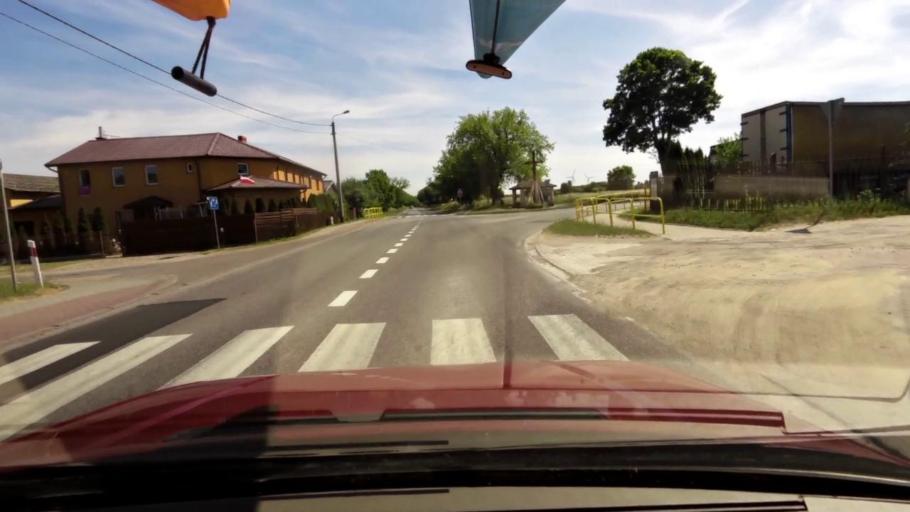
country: PL
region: Pomeranian Voivodeship
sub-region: Powiat slupski
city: Kobylnica
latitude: 54.4115
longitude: 17.0078
